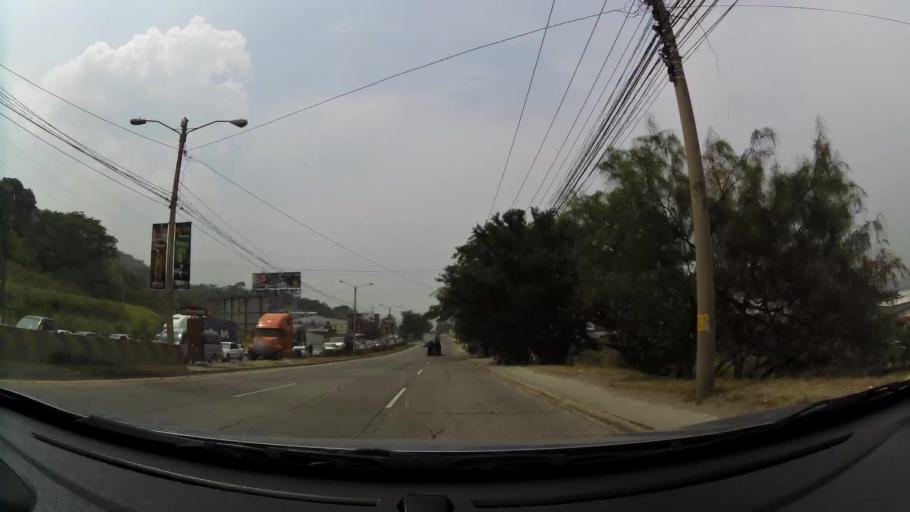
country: HN
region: Cortes
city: Chotepe
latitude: 15.4376
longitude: -88.0208
